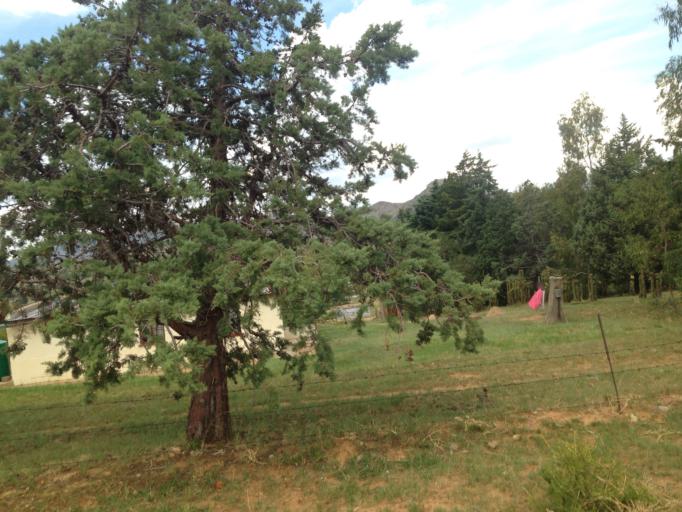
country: LS
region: Mafeteng
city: Mafeteng
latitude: -29.6932
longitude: 27.4322
